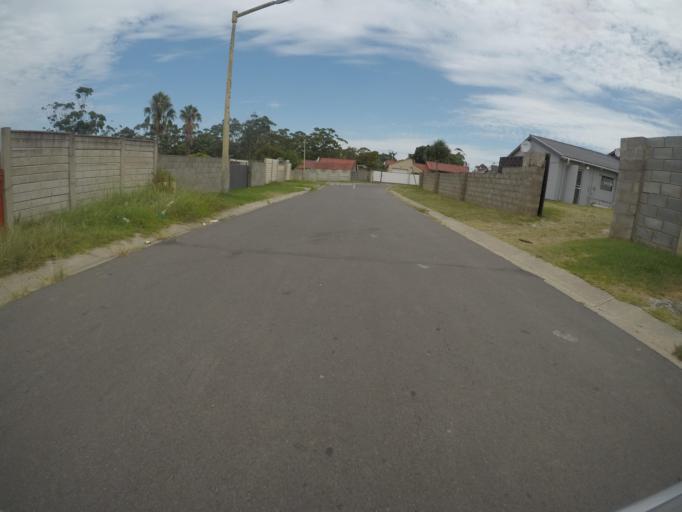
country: ZA
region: Eastern Cape
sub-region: Buffalo City Metropolitan Municipality
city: East London
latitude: -32.9933
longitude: 27.8806
